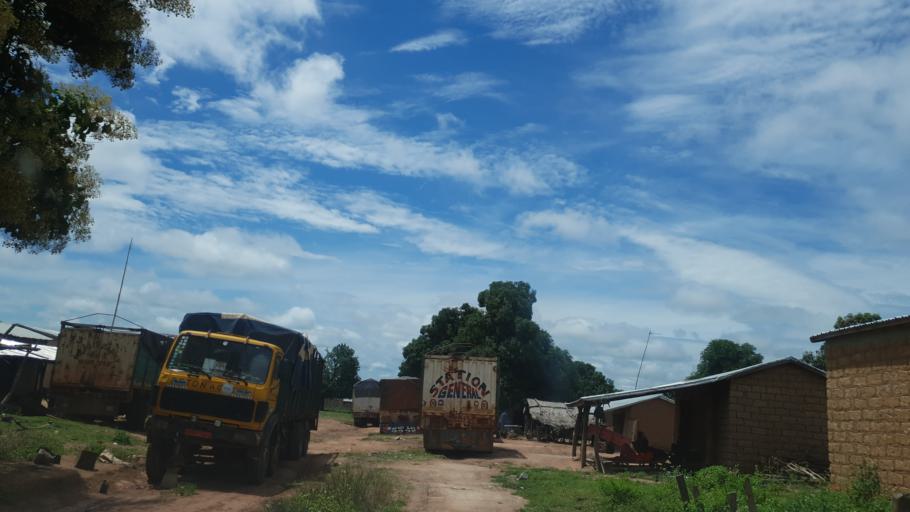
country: CI
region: Savanes
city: Tengrela
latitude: 10.3608
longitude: -6.9193
